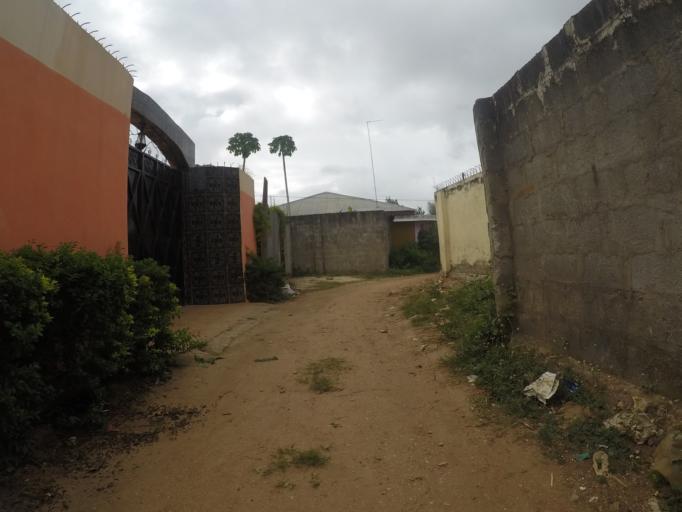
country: TZ
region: Zanzibar Urban/West
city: Zanzibar
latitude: -6.2136
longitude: 39.2159
